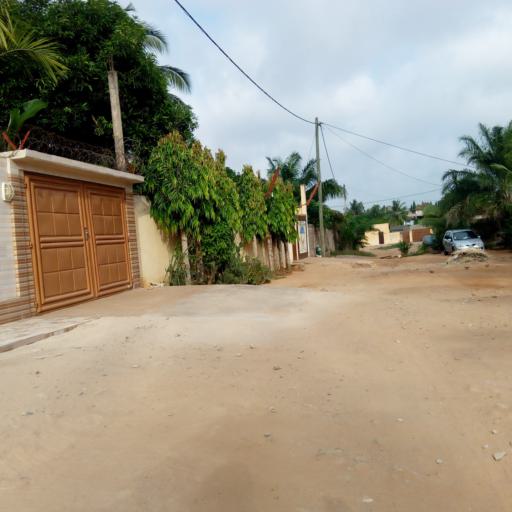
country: TG
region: Maritime
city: Lome
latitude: 6.1720
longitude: 1.1786
